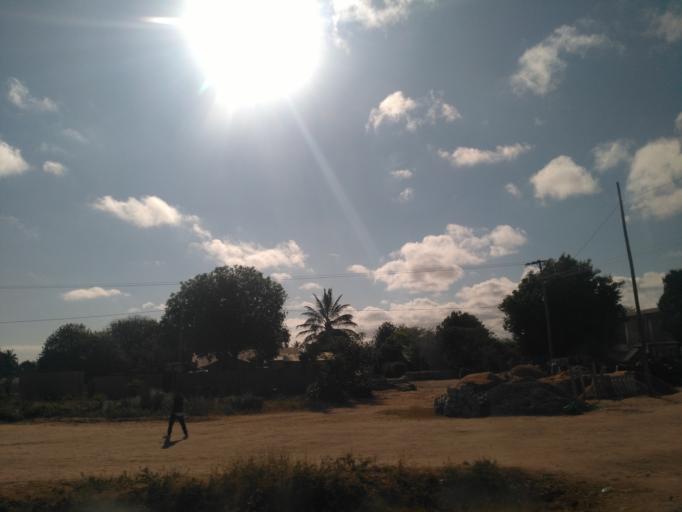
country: TZ
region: Dodoma
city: Dodoma
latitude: -6.1839
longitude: 35.7324
